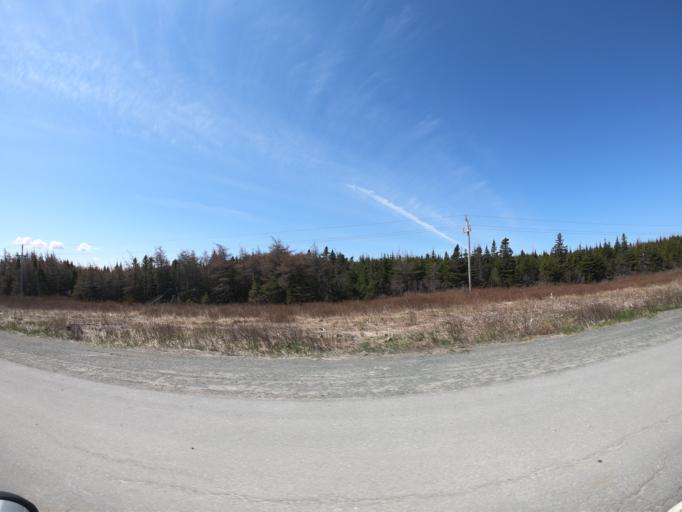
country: CA
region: Newfoundland and Labrador
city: Mount Pearl
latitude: 47.5021
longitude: -52.8183
